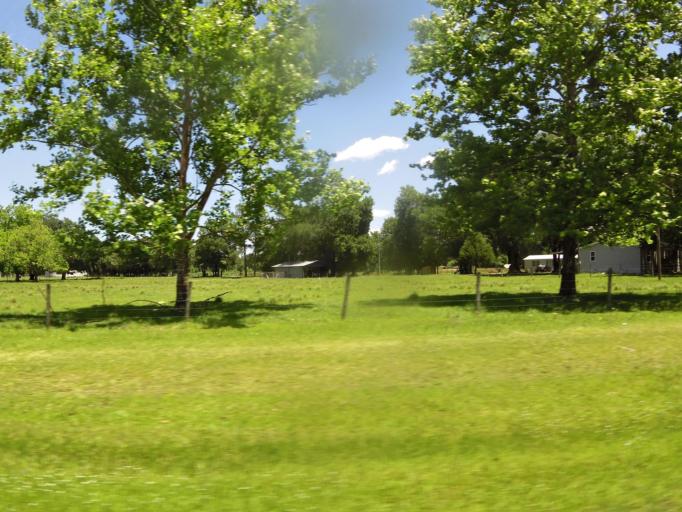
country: US
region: Florida
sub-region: Union County
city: Lake Butler
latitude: 30.0285
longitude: -82.2123
